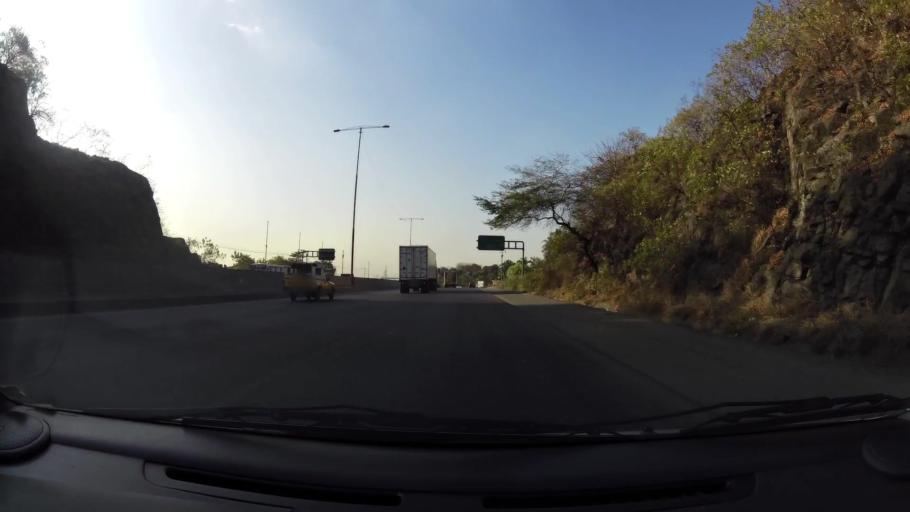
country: EC
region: Guayas
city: Santa Lucia
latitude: -2.1523
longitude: -79.9466
